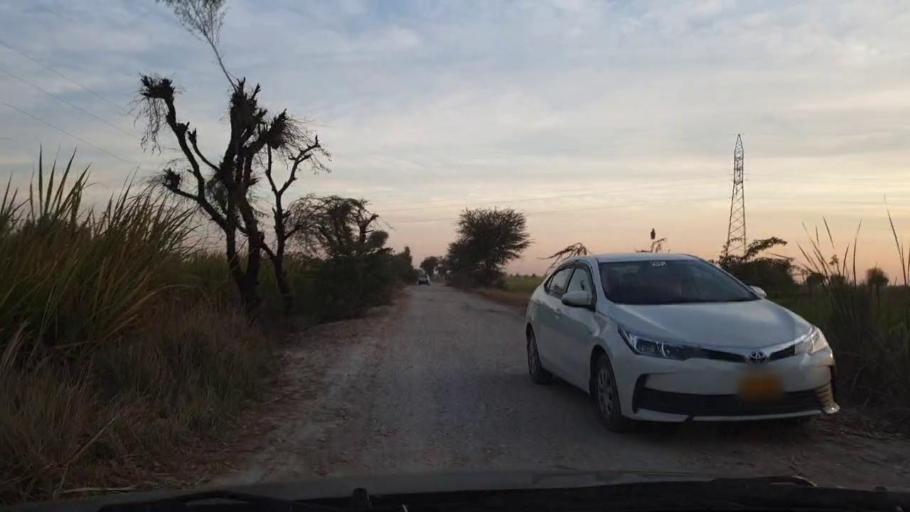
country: PK
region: Sindh
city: Sinjhoro
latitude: 26.1142
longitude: 68.7963
